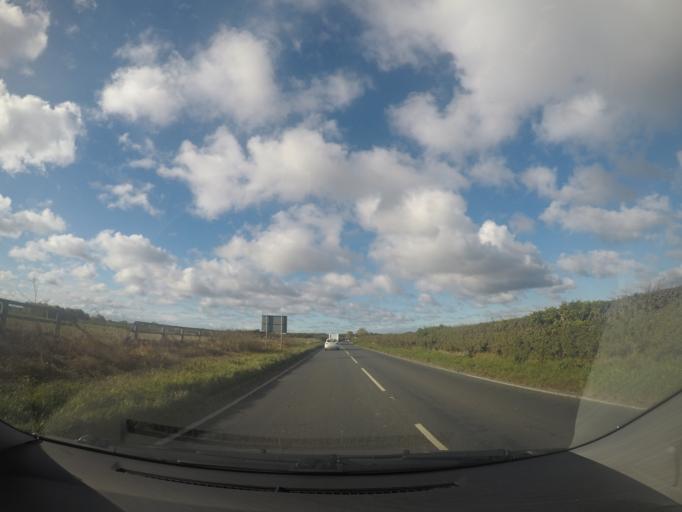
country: GB
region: England
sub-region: City of York
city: Nether Poppleton
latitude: 53.9751
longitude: -1.1649
